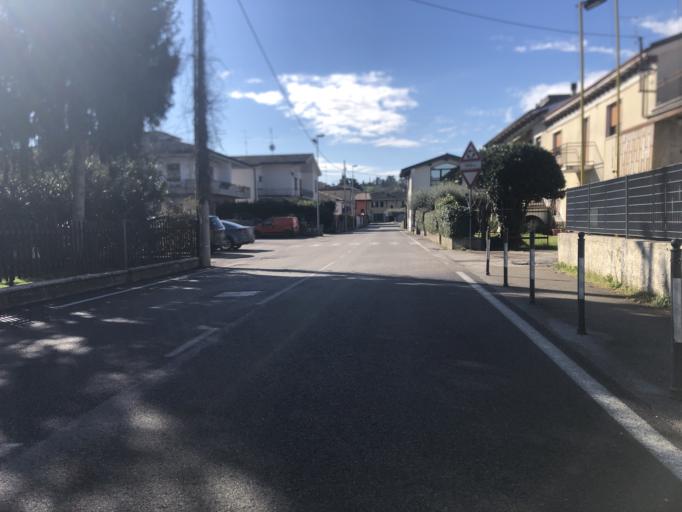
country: IT
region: Veneto
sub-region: Provincia di Verona
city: Bussolengo
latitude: 45.4828
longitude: 10.8465
